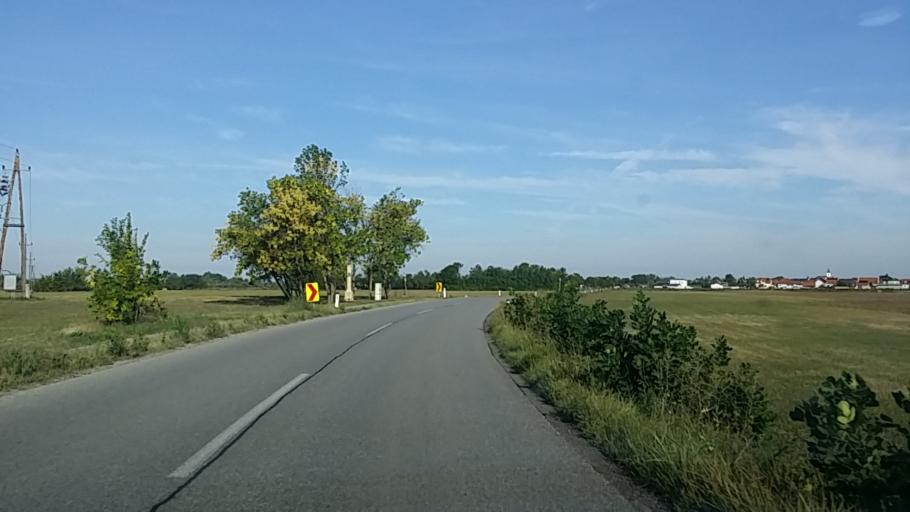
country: AT
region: Burgenland
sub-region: Politischer Bezirk Neusiedl am See
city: Apetlon
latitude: 47.7328
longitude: 16.8390
